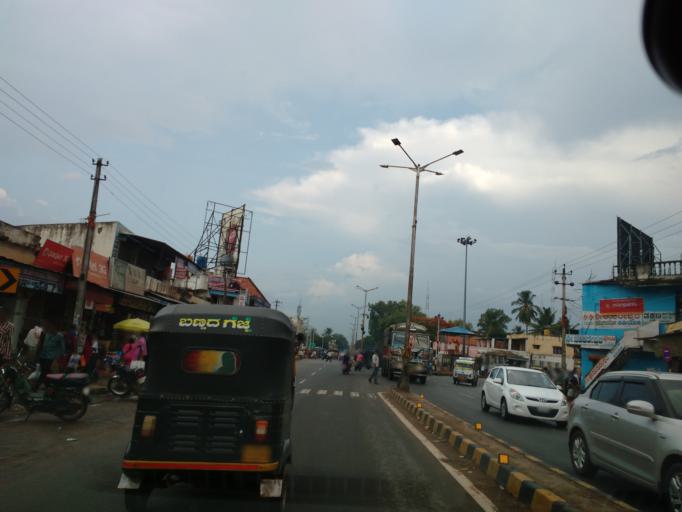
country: IN
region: Karnataka
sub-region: Hassan
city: Arsikere
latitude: 13.3137
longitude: 76.2563
